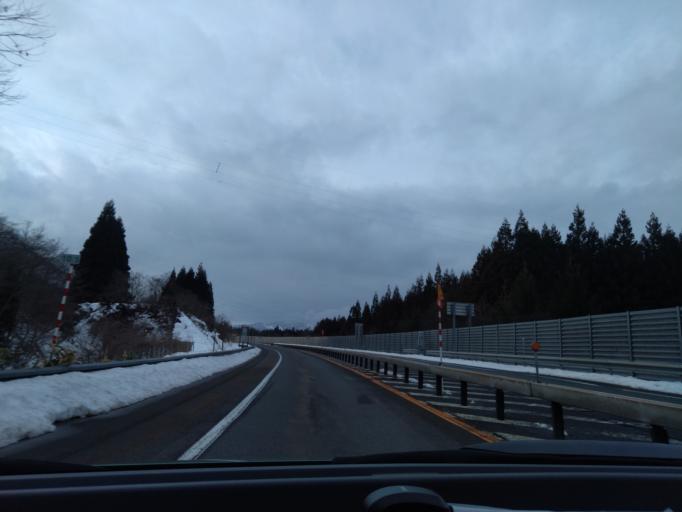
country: JP
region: Iwate
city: Kitakami
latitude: 39.2954
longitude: 140.9667
